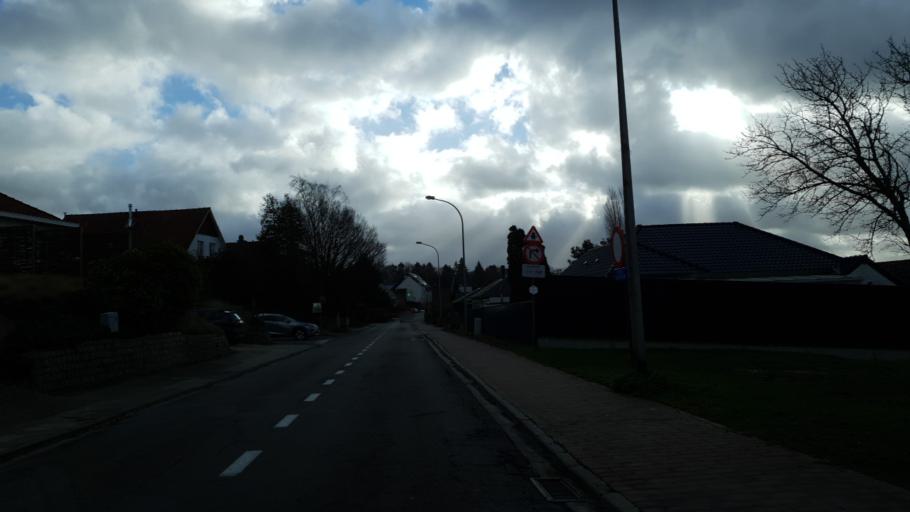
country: BE
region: Flanders
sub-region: Provincie Vlaams-Brabant
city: Tervuren
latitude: 50.8401
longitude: 4.5382
